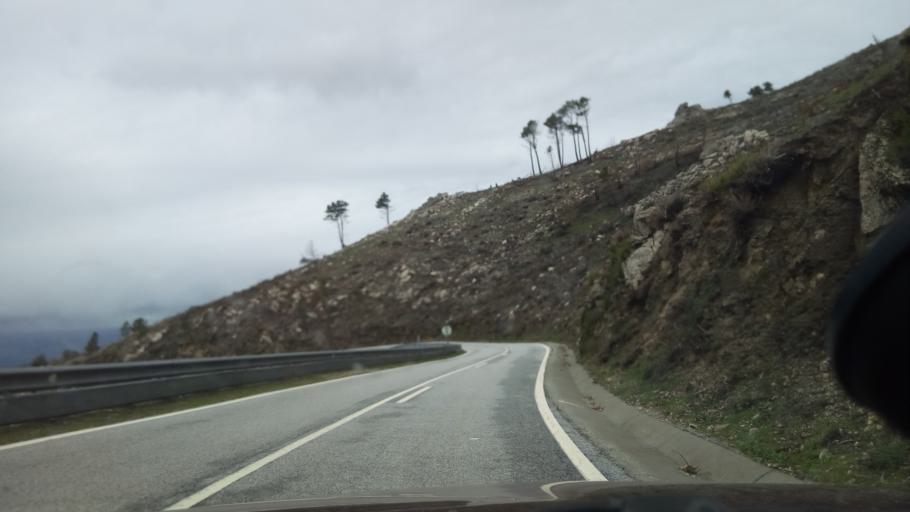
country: PT
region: Guarda
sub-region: Manteigas
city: Manteigas
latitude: 40.4524
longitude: -7.5857
